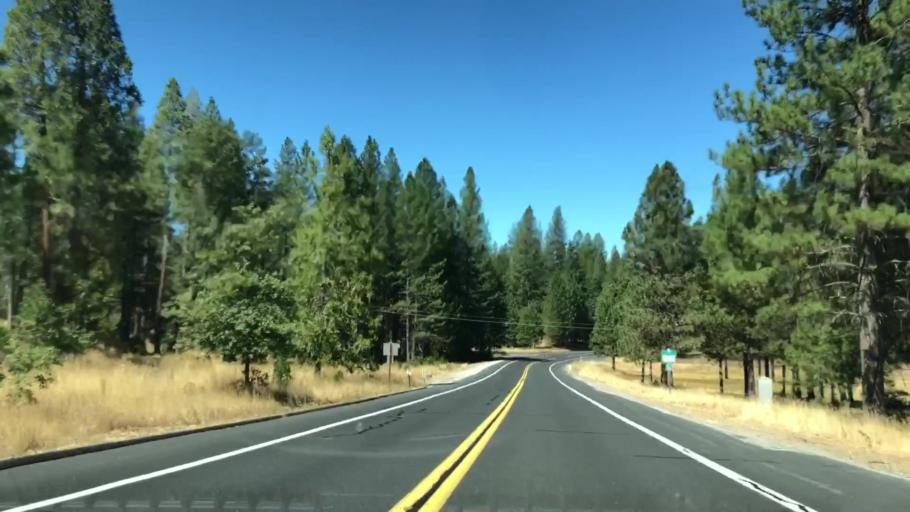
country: US
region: California
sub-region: Tuolumne County
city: Tuolumne City
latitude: 37.8165
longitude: -120.1274
